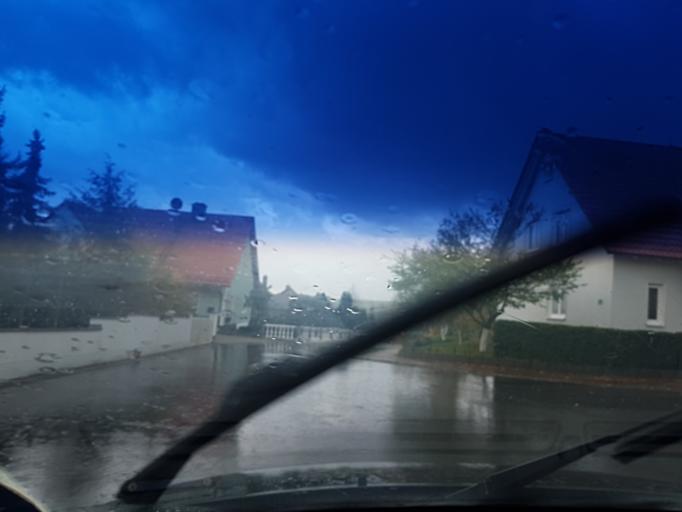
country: DE
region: Bavaria
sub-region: Regierungsbezirk Mittelfranken
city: Burghaslach
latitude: 49.7368
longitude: 10.6090
